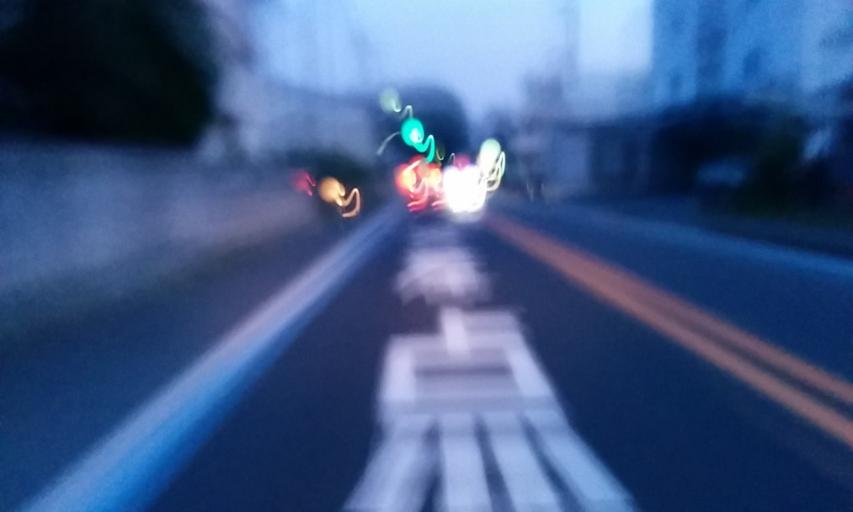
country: JP
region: Ehime
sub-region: Nishiuwa-gun
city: Ikata-cho
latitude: 33.4927
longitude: 132.3974
